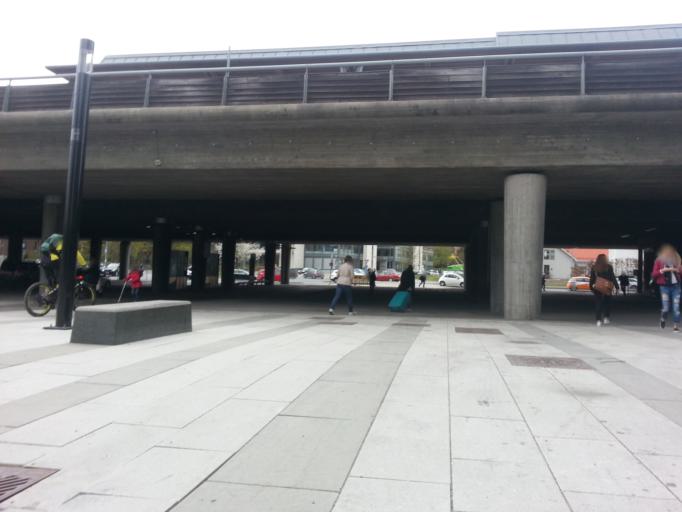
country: NO
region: Oslo
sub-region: Oslo
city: Sjolyststranda
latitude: 59.9219
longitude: 10.6795
